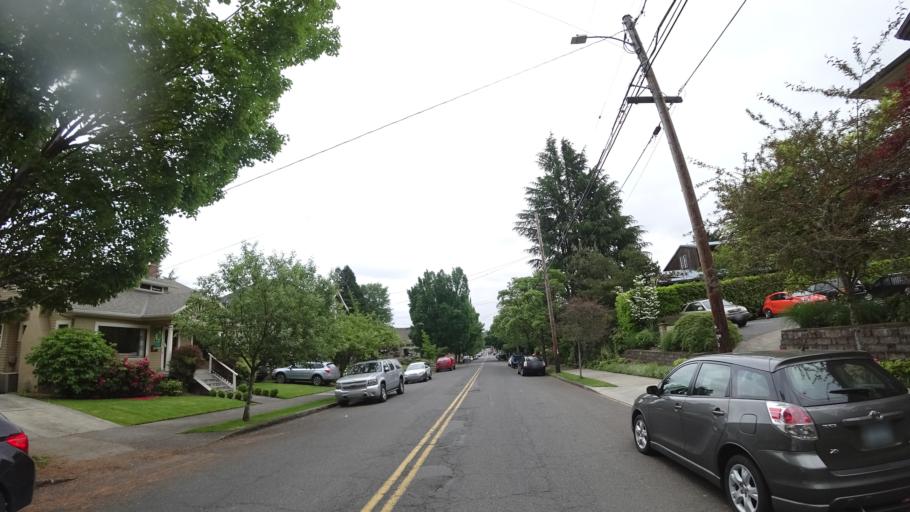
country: US
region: Oregon
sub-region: Multnomah County
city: Portland
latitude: 45.4773
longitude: -122.6762
